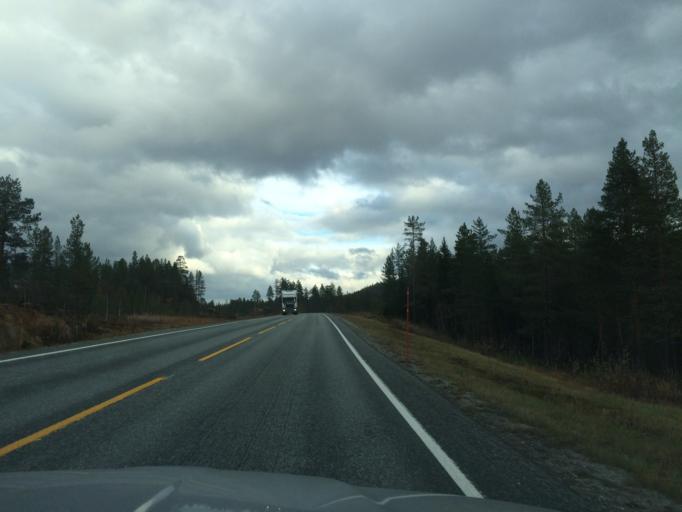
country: NO
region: Nord-Trondelag
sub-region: Namsskogan
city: Namsskogan
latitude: 64.7638
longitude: 12.8685
